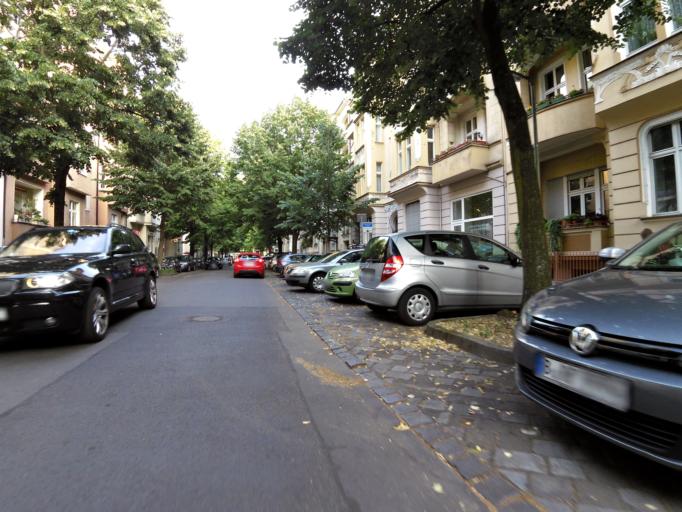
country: DE
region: Berlin
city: Steglitz Bezirk
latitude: 52.4600
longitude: 13.3211
